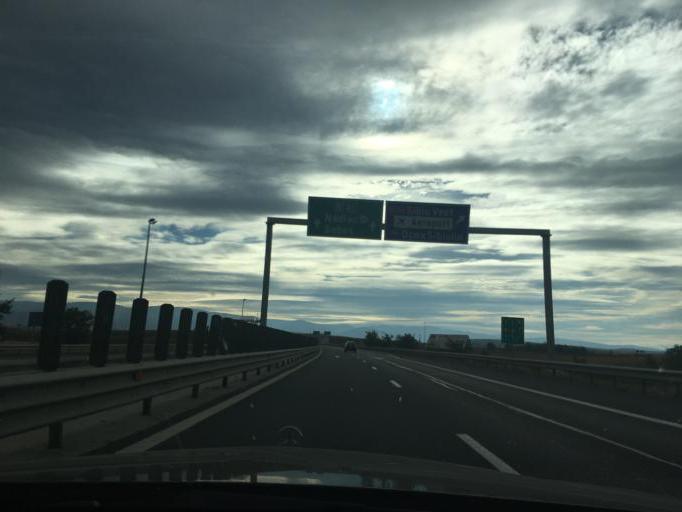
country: RO
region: Sibiu
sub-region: Comuna Sura Mica
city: Sura Mica
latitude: 45.8227
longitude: 24.0791
